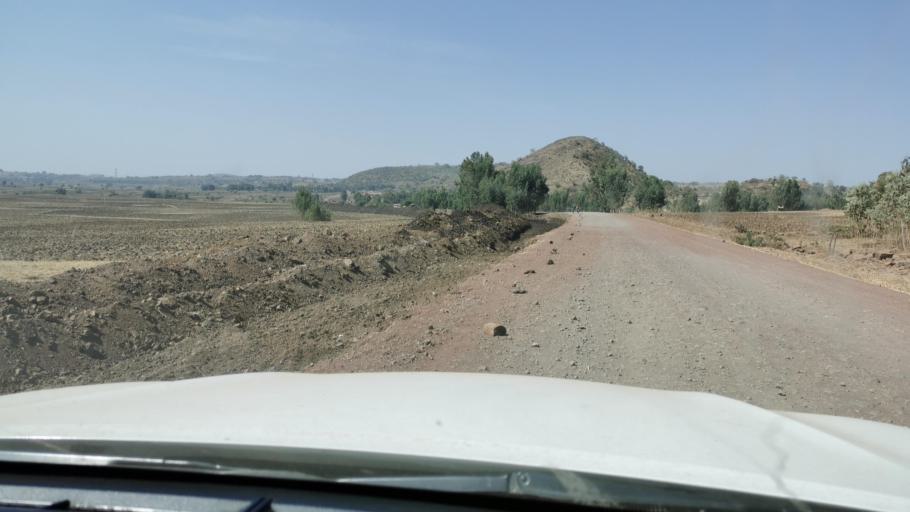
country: ET
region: Amhara
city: Bahir Dar
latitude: 11.8440
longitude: 37.0030
